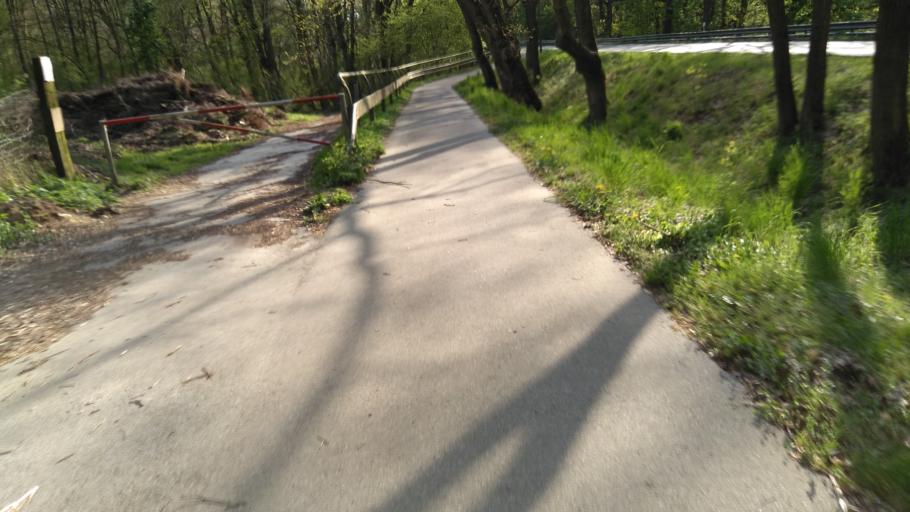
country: DE
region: Lower Saxony
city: Buxtehude
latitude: 53.4390
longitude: 9.6595
